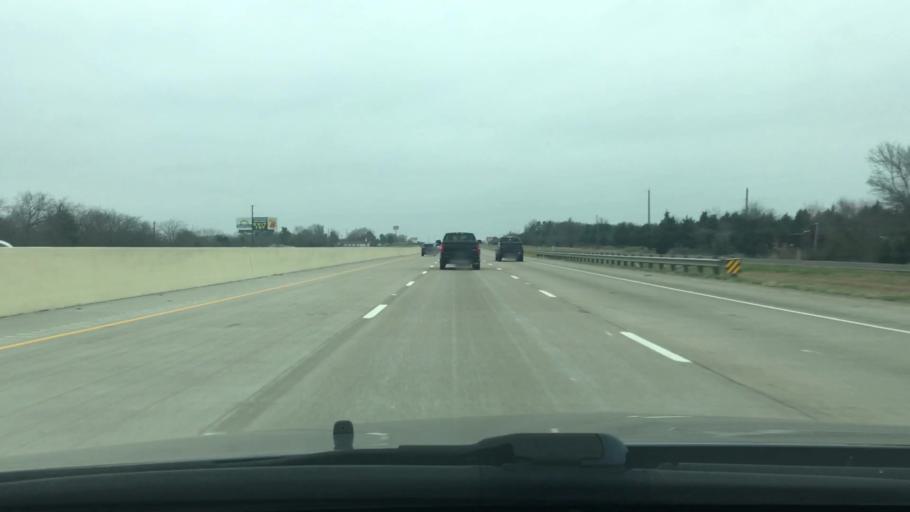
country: US
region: Texas
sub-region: Navarro County
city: Corsicana
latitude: 31.9986
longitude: -96.4300
